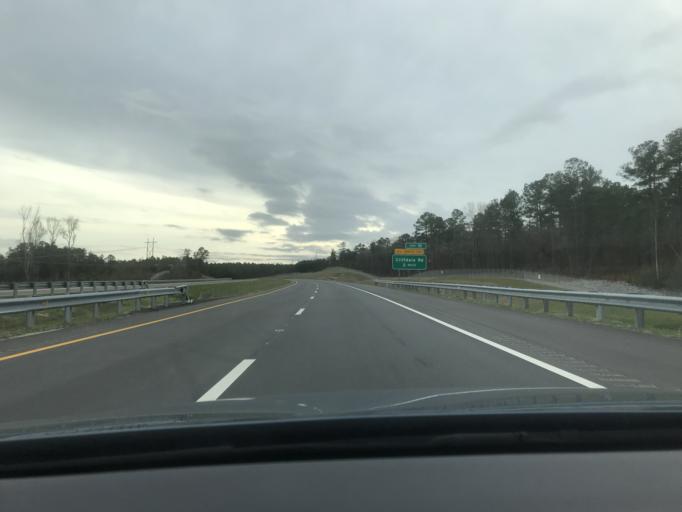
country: US
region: North Carolina
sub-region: Cumberland County
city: Fort Bragg
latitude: 35.0977
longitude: -79.0251
